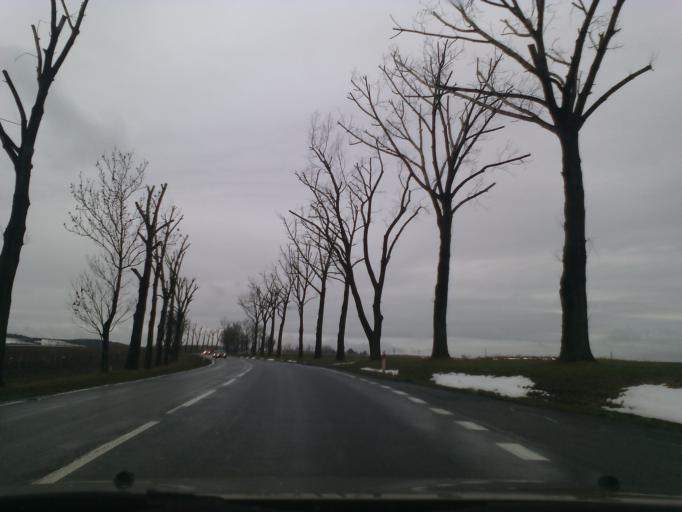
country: PL
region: Lower Silesian Voivodeship
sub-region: Powiat swidnicki
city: Swiebodzice
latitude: 50.8457
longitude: 16.3909
